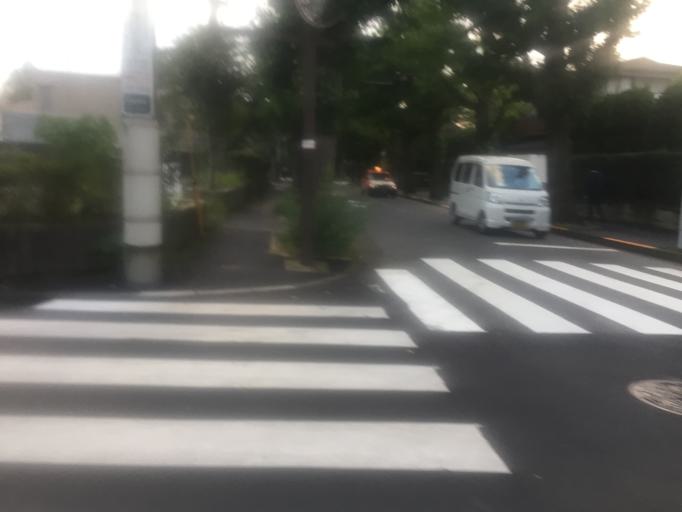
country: JP
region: Kanagawa
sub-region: Kawasaki-shi
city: Kawasaki
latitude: 35.5960
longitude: 139.6657
